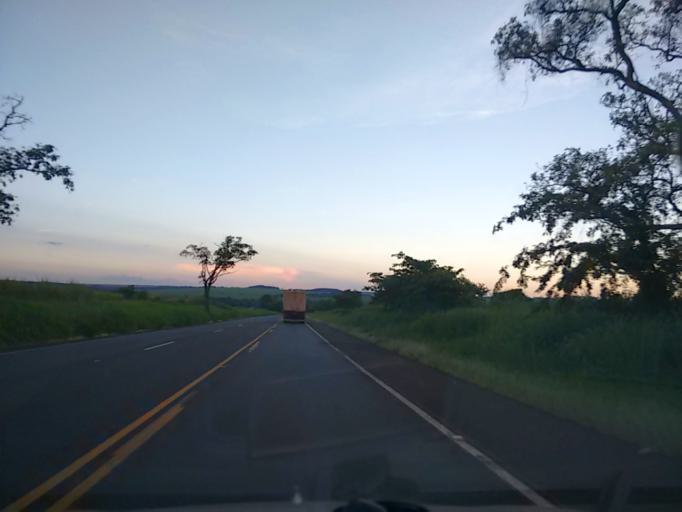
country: BR
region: Sao Paulo
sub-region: Boa Esperanca Do Sul
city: Boa Esperanca do Sul
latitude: -22.0904
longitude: -48.4483
